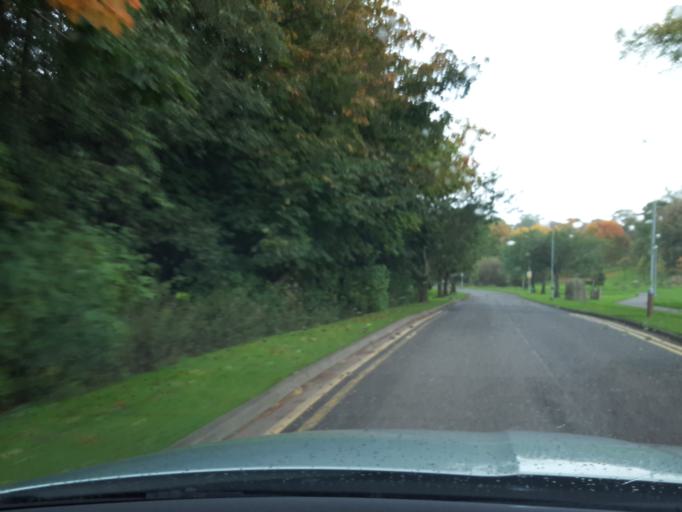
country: GB
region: Scotland
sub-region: West Lothian
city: Bathgate
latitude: 55.9090
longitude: -3.6416
